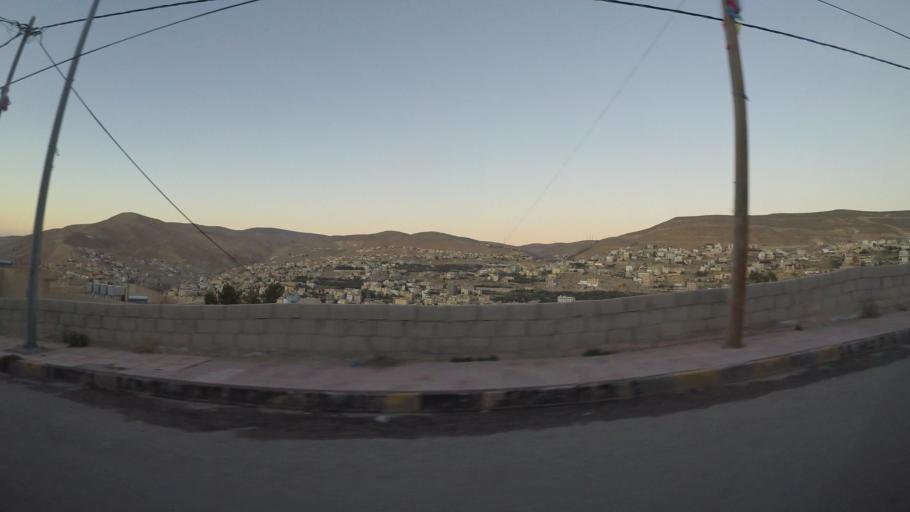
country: JO
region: Ma'an
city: Petra
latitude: 30.3173
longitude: 35.4751
